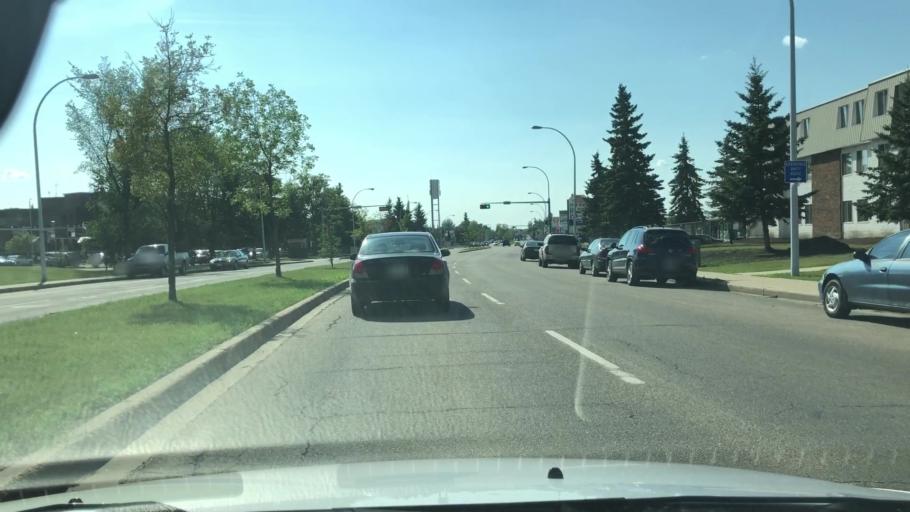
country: CA
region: Alberta
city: Edmonton
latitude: 53.6058
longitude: -113.4811
